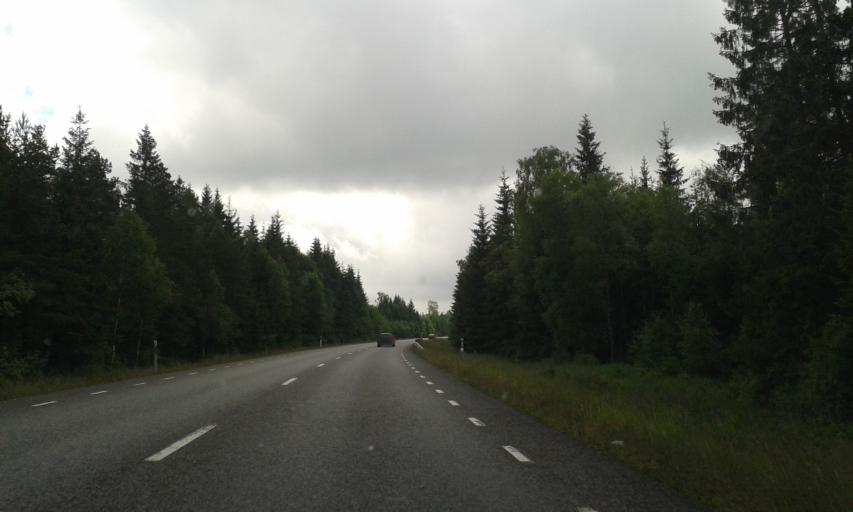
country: SE
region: Joenkoeping
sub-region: Gislaveds Kommun
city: Gislaved
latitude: 57.3951
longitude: 13.4662
